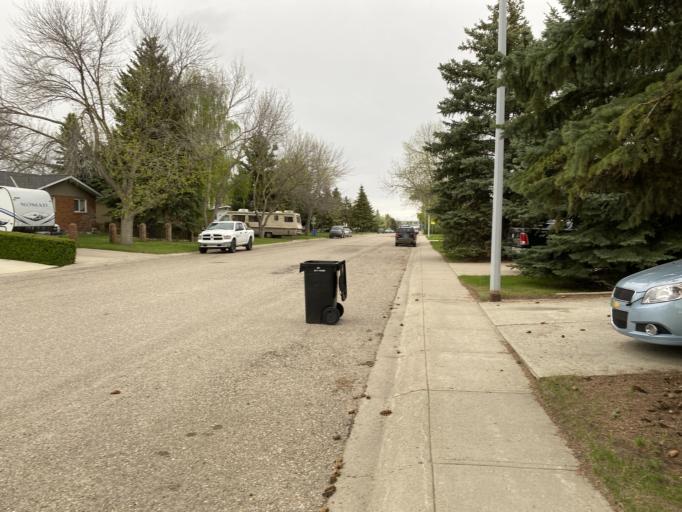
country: CA
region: Alberta
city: Nanton
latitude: 50.3427
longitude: -113.7756
